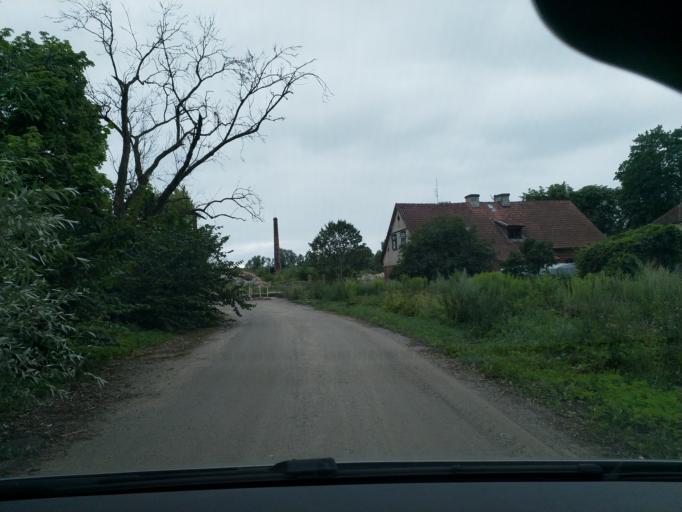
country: LV
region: Kuldigas Rajons
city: Kuldiga
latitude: 56.9646
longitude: 21.9780
